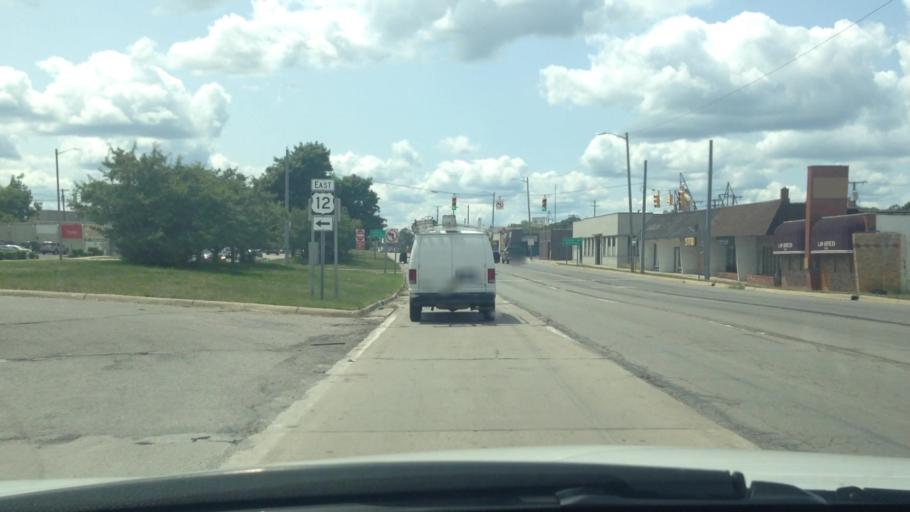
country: US
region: Michigan
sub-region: Wayne County
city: Inkster
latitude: 42.2948
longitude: -83.3071
